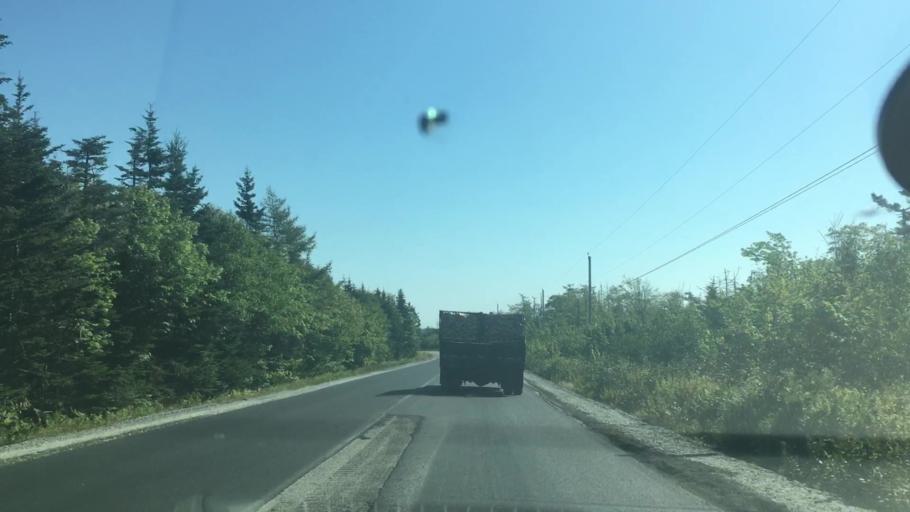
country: CA
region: Nova Scotia
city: New Glasgow
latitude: 44.8987
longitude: -62.4337
